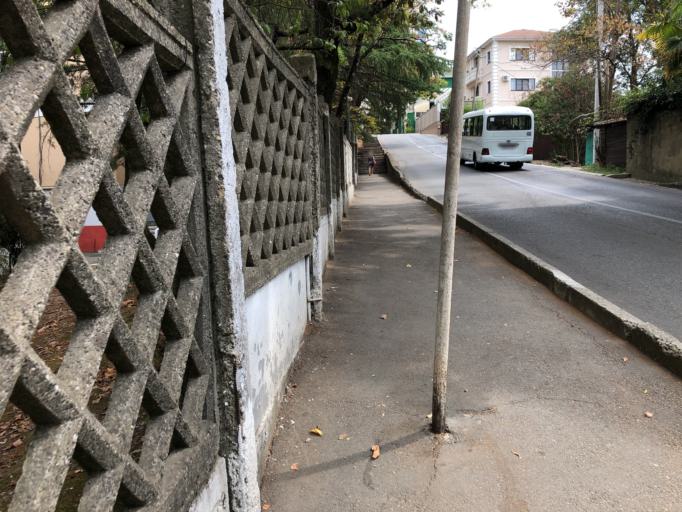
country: RU
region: Krasnodarskiy
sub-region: Sochi City
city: Sochi
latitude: 43.5918
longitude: 39.7359
